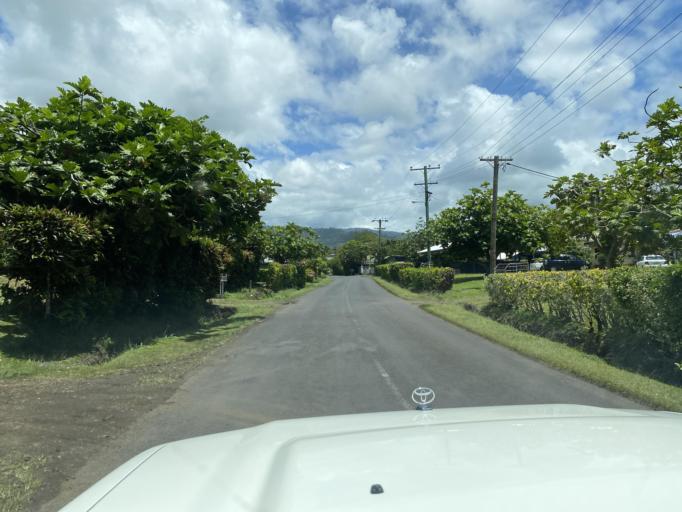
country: WS
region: Tuamasaga
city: Apia
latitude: -13.8465
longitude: -171.7776
